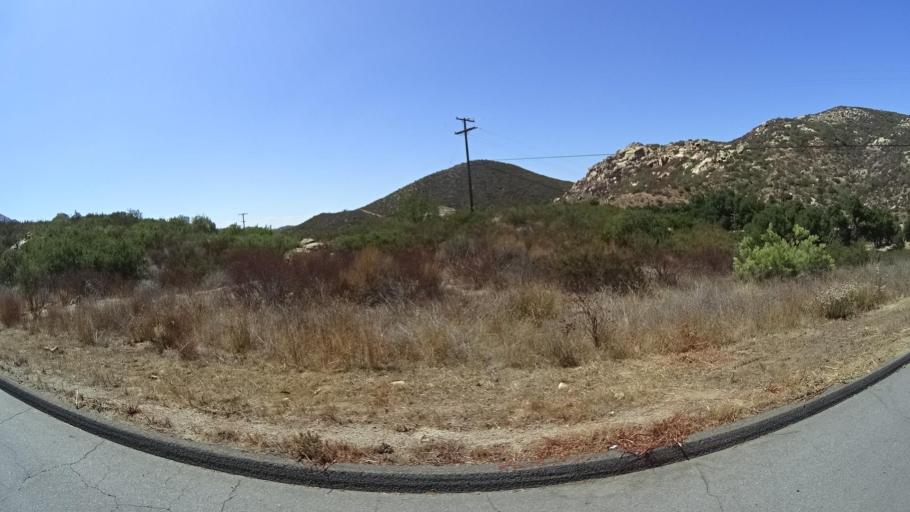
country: US
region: California
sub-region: San Diego County
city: San Diego Country Estates
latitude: 32.9518
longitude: -116.8388
